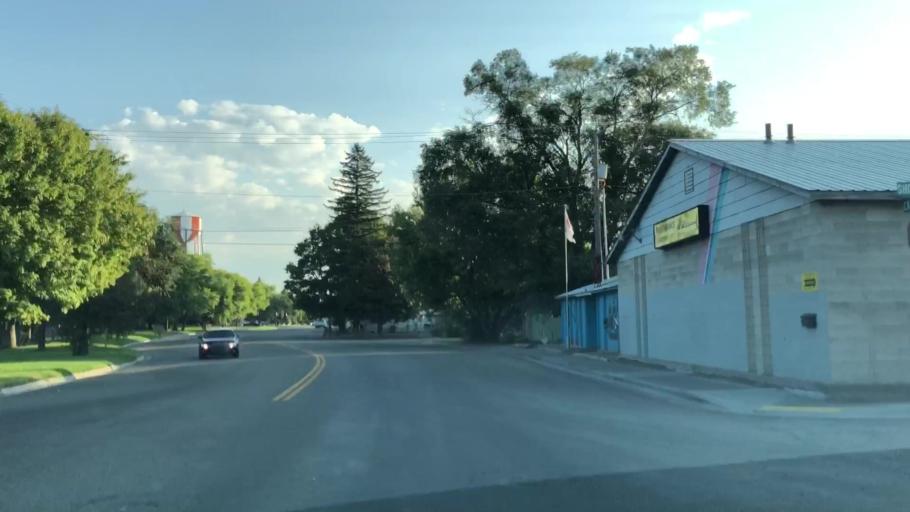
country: US
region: Idaho
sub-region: Bonneville County
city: Idaho Falls
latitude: 43.4876
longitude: -112.0459
